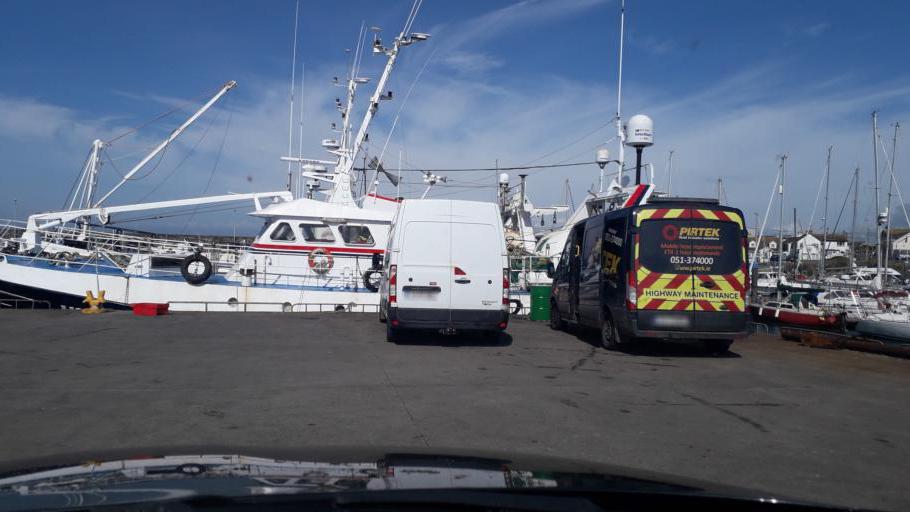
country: IE
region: Leinster
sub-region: Loch Garman
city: Loch Garman
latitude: 52.1720
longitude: -6.5870
